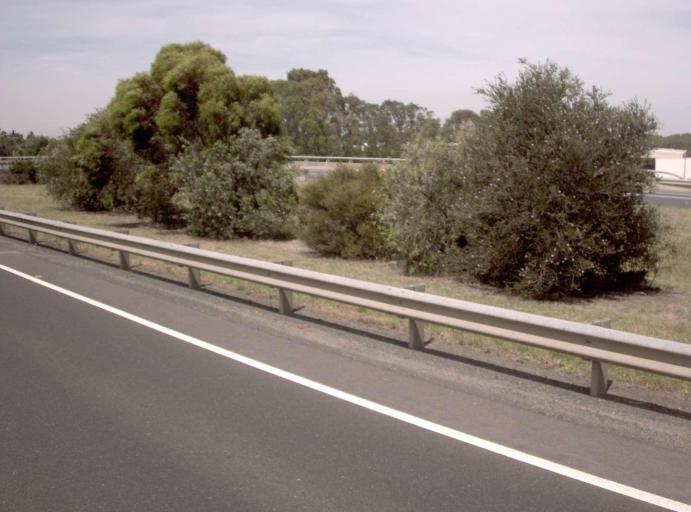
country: AU
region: Victoria
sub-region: Casey
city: Hampton Park
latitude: -38.0356
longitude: 145.2473
